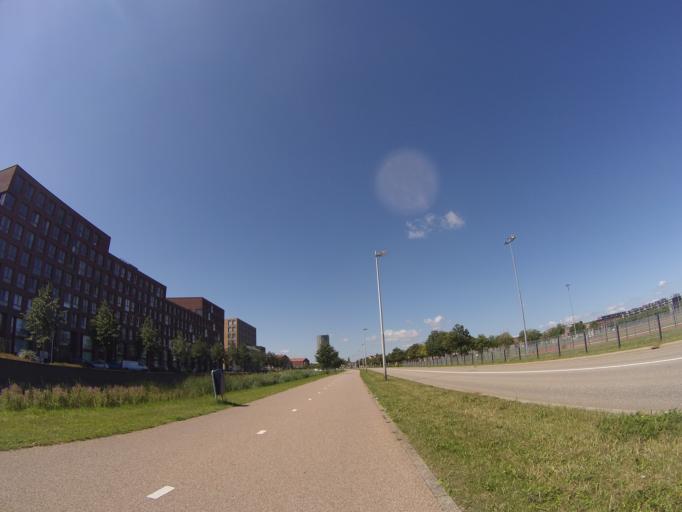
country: NL
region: Utrecht
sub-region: Stichtse Vecht
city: Maarssen
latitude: 52.0905
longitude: 5.0576
